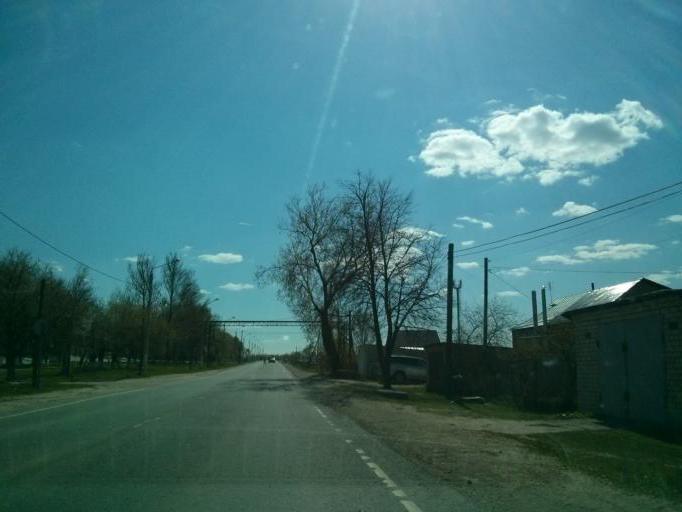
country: RU
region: Nizjnij Novgorod
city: Taremskoye
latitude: 55.9268
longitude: 43.0382
